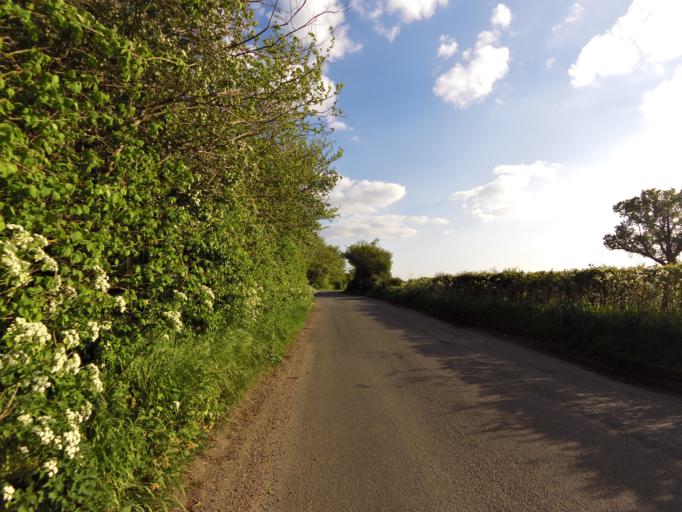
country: GB
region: England
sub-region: Suffolk
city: Halesworth
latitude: 52.3980
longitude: 1.5390
